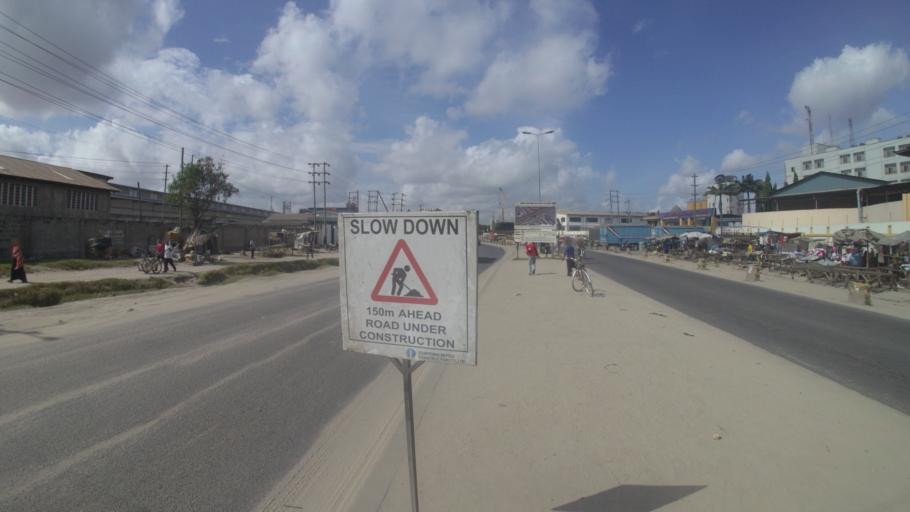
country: TZ
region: Dar es Salaam
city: Dar es Salaam
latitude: -6.8418
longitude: 39.2451
